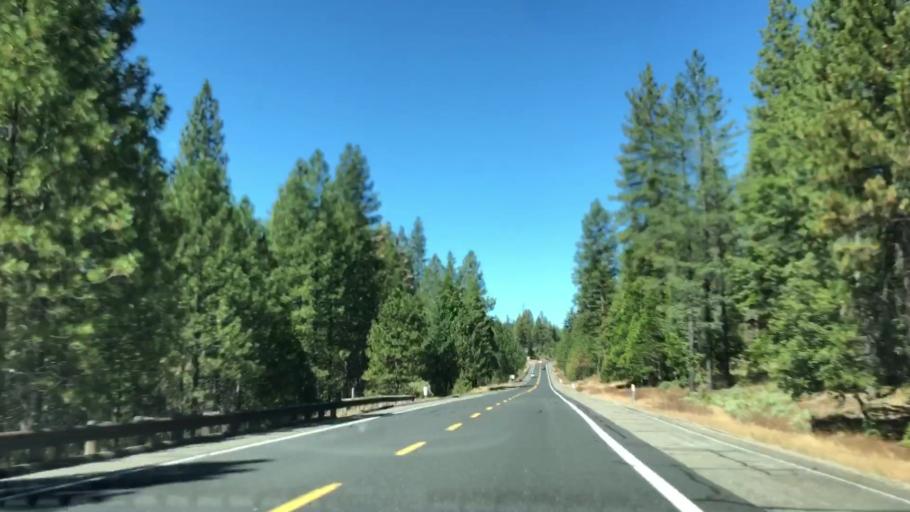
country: US
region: California
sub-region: Tuolumne County
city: Tuolumne City
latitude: 37.8218
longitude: -120.1623
